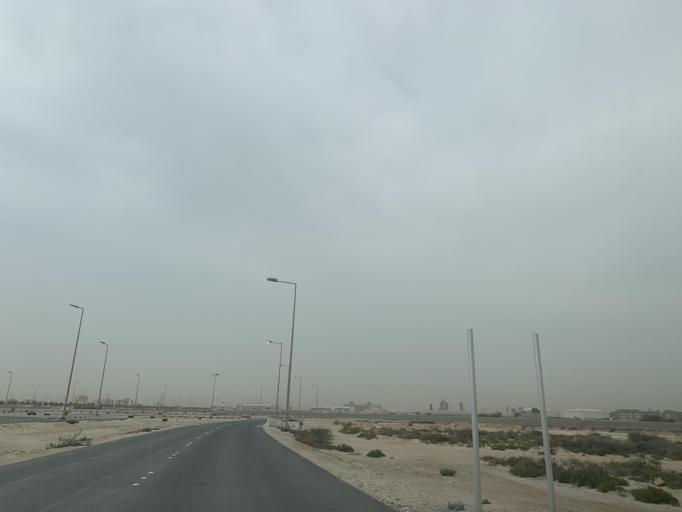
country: BH
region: Northern
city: Madinat `Isa
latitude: 26.1829
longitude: 50.5078
